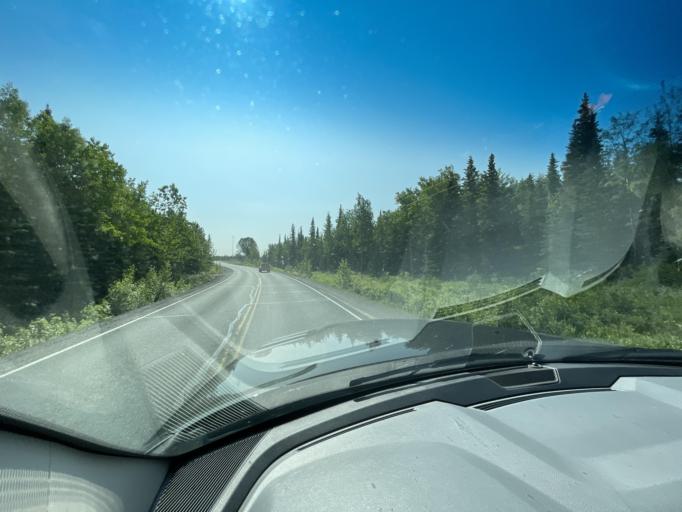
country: US
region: Alaska
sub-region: Kenai Peninsula Borough
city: Cohoe
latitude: 60.3000
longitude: -151.2825
